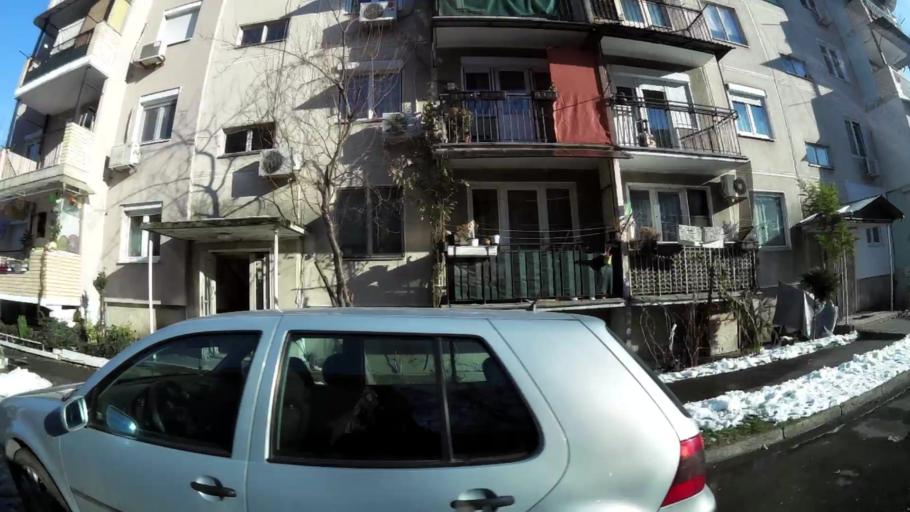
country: MK
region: Karpos
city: Skopje
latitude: 42.0063
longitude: 21.3946
